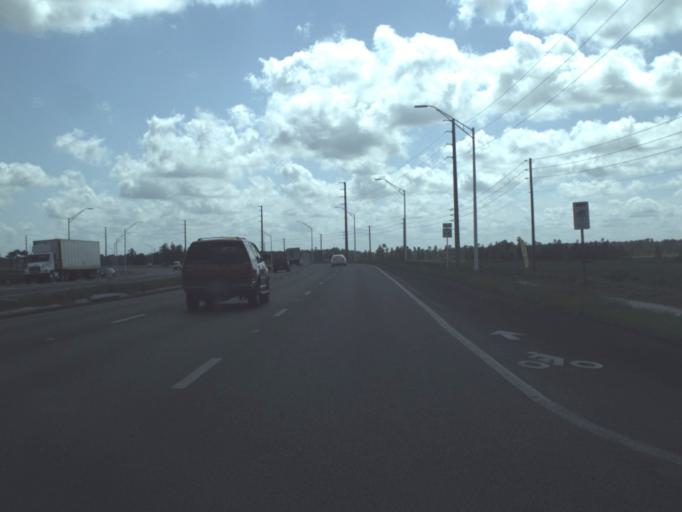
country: US
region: Florida
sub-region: Hillsborough County
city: Cheval
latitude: 28.1934
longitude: -82.5052
